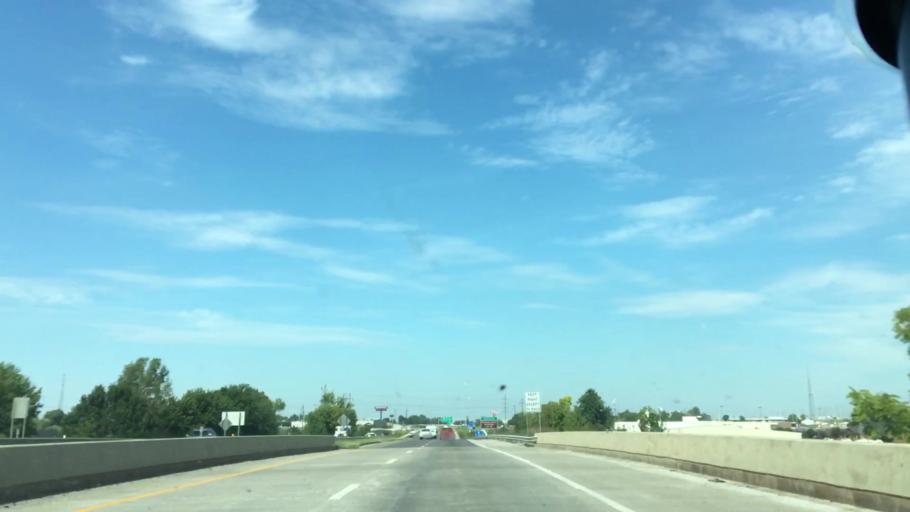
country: US
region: Kentucky
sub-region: Daviess County
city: Owensboro
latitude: 37.7462
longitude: -87.0713
